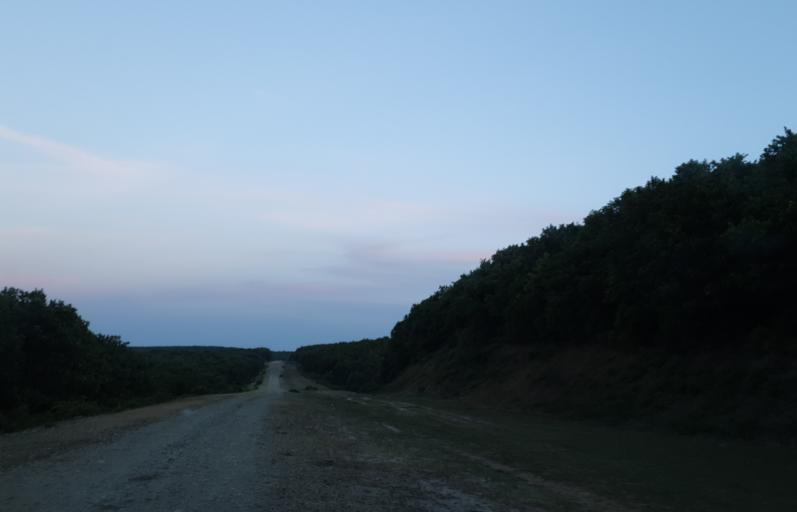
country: TR
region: Kirklareli
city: Salmydessus
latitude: 41.6777
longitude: 28.0895
